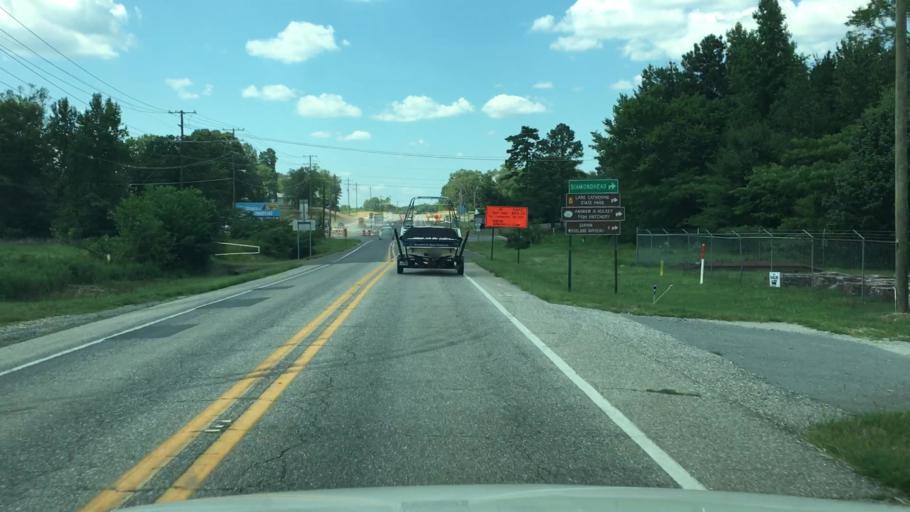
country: US
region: Arkansas
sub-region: Garland County
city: Lake Hamilton
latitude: 34.4117
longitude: -93.0940
